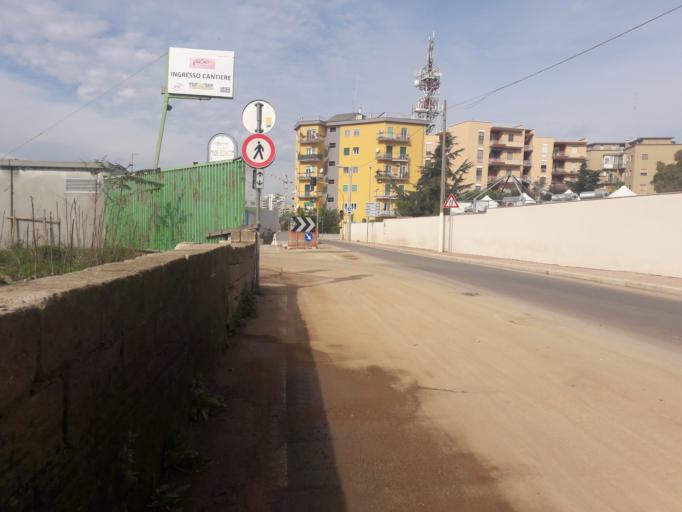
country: IT
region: Apulia
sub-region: Provincia di Bari
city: Bari
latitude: 41.1131
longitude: 16.8873
